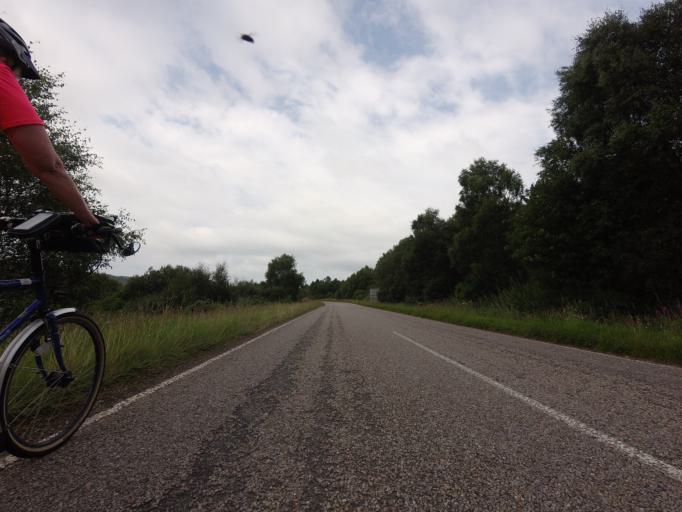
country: GB
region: Scotland
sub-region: Highland
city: Evanton
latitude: 57.9364
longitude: -4.4050
